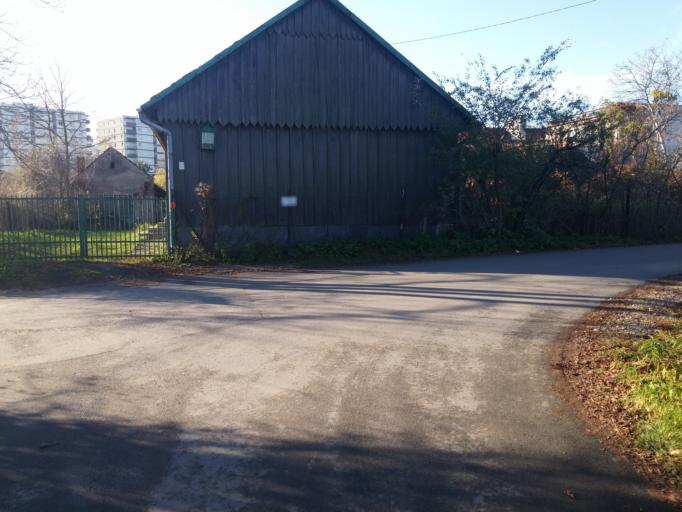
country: PL
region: Lesser Poland Voivodeship
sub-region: Powiat krakowski
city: Ochojno
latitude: 50.0126
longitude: 19.9822
